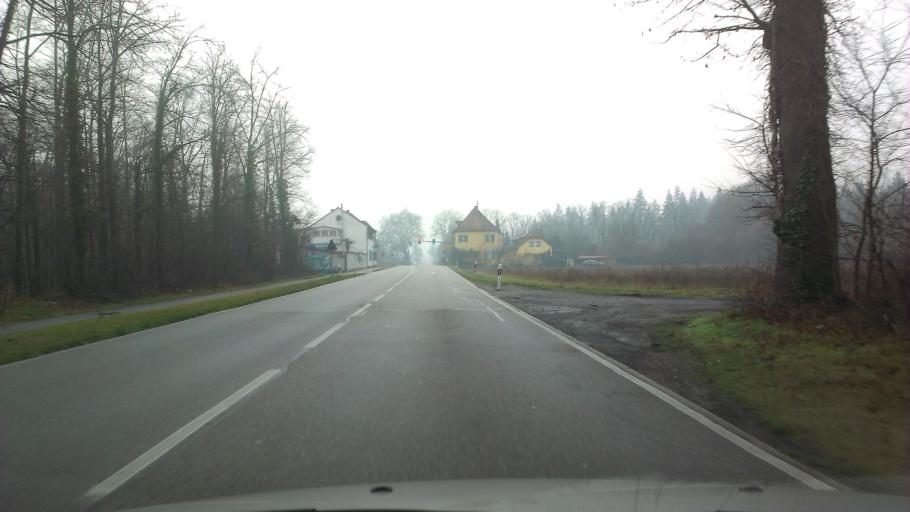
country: DE
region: Baden-Wuerttemberg
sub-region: Karlsruhe Region
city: Graben-Neudorf
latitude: 49.1931
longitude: 8.5081
